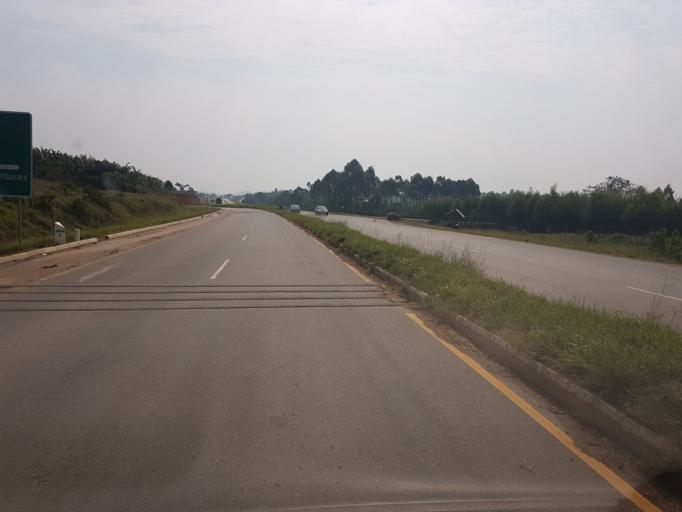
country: UG
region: Western Region
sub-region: Mbarara District
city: Bwizibwera
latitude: -0.6338
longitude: 30.5980
